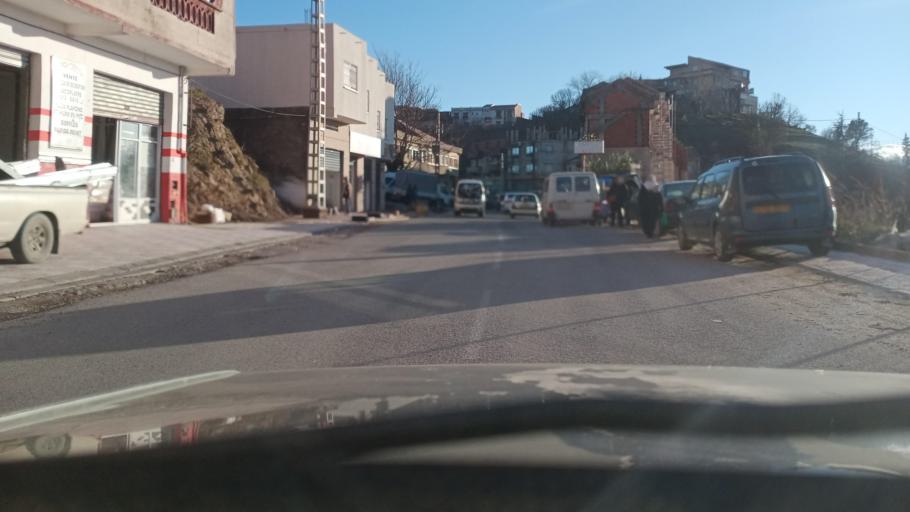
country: DZ
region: Tizi Ouzou
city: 'Ain el Hammam
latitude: 36.5615
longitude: 4.3242
